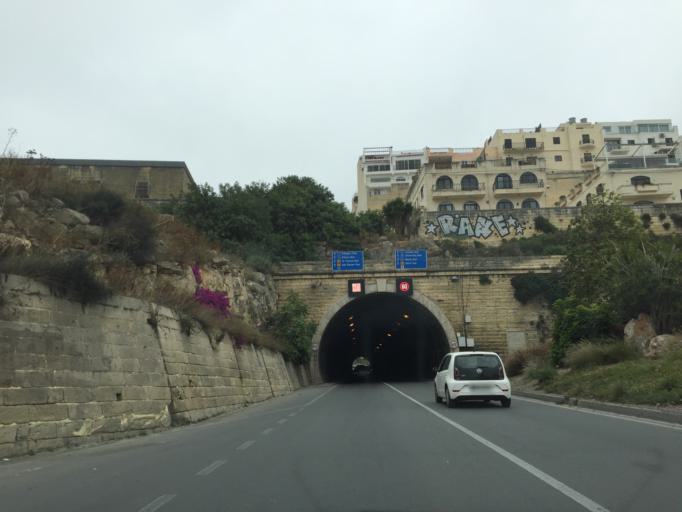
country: MT
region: Saint Julian
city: San Giljan
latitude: 35.9153
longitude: 14.4863
